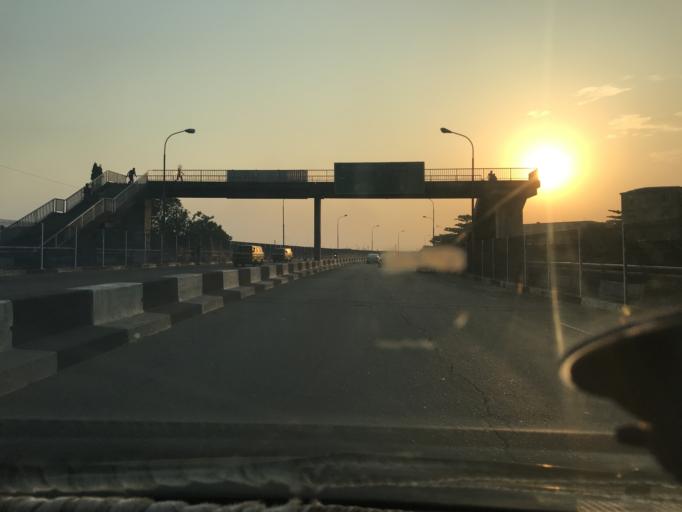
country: NG
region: Lagos
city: Makoko
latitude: 6.4924
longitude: 3.3864
